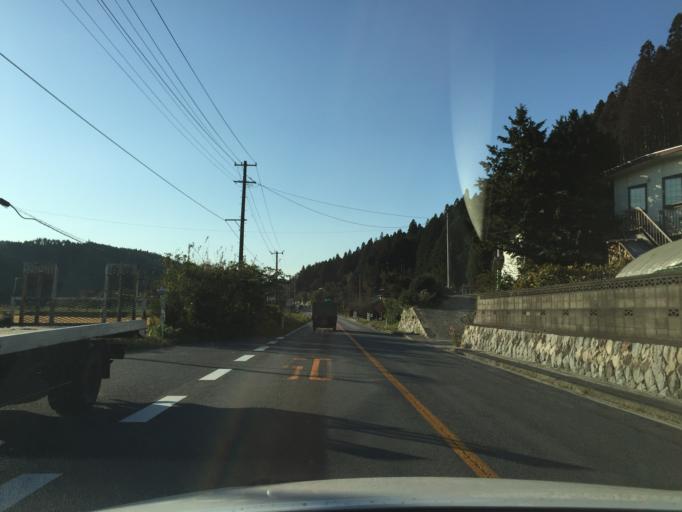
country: JP
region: Fukushima
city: Iwaki
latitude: 37.1108
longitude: 140.7624
